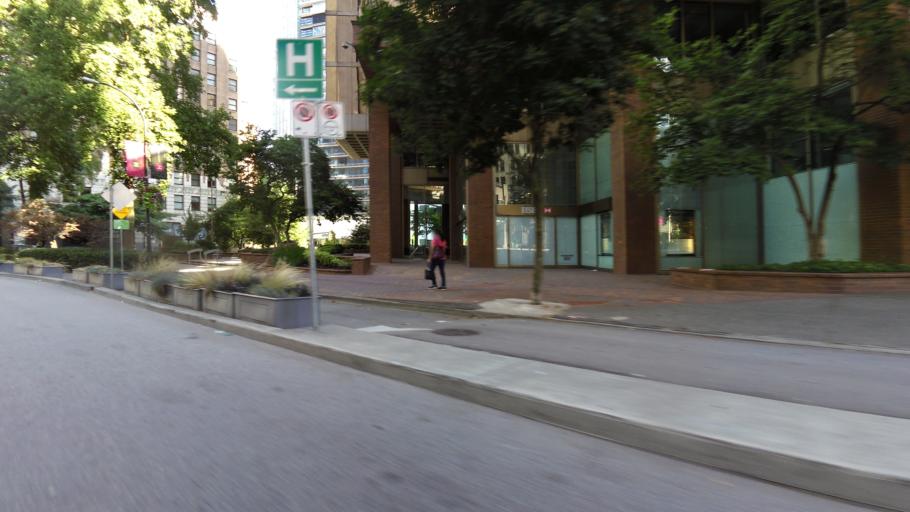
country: CA
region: British Columbia
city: West End
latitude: 49.2868
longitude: -123.1161
